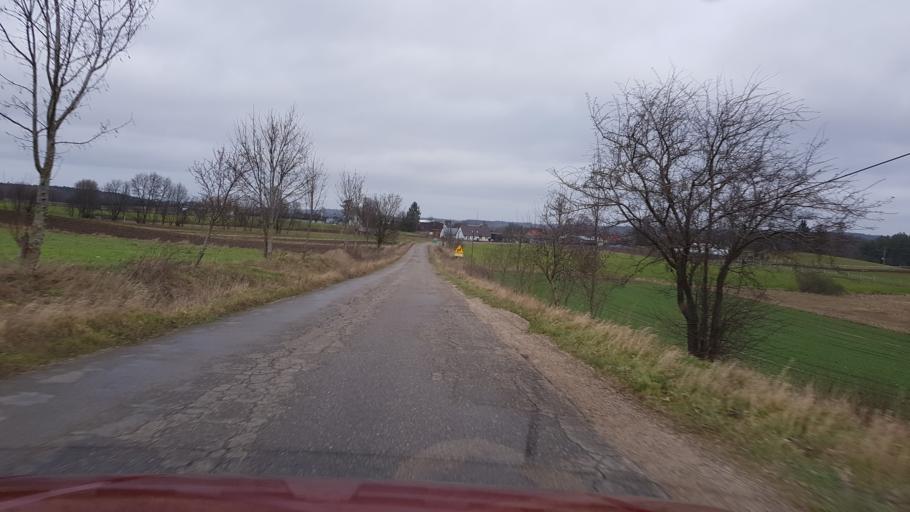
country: PL
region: Pomeranian Voivodeship
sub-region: Powiat bytowski
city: Borzytuchom
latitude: 54.1764
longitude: 17.3555
